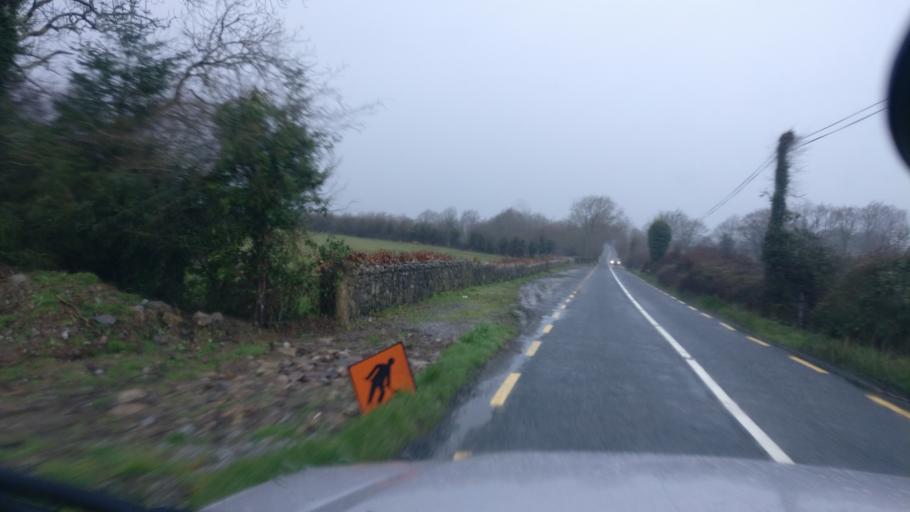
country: IE
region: Connaught
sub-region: County Galway
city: Loughrea
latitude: 53.1544
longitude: -8.4794
